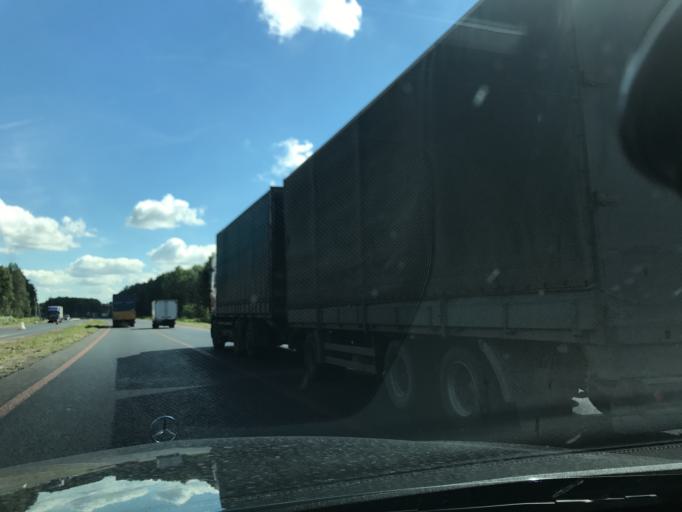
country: RU
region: Nizjnij Novgorod
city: Gorbatovka
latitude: 56.2471
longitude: 43.7165
